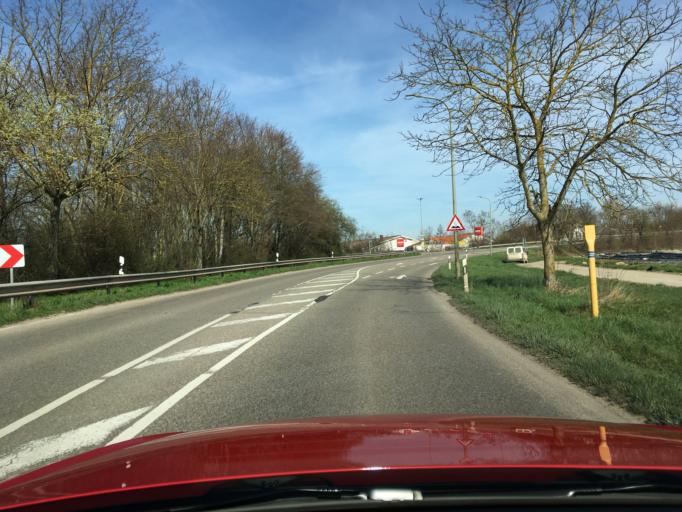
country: DE
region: Rheinland-Pfalz
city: Bohl-Iggelheim
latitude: 49.3763
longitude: 8.3055
